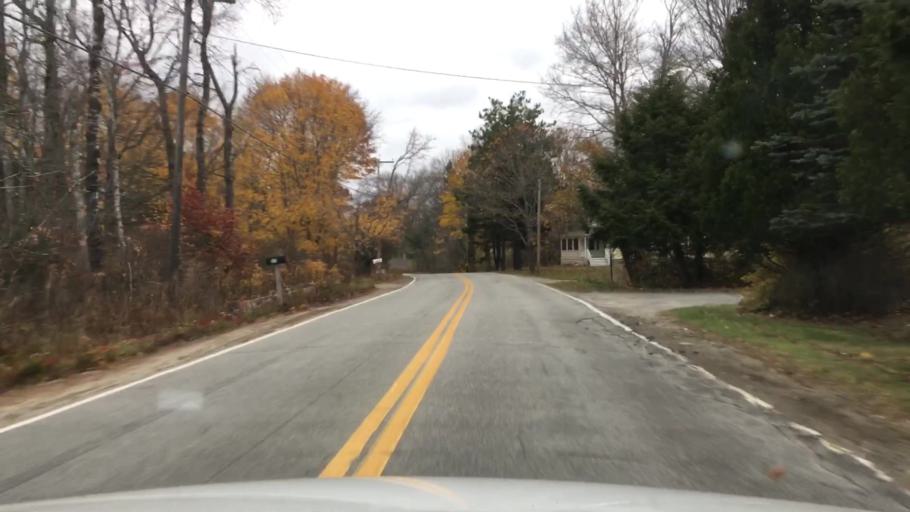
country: US
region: Maine
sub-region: Hancock County
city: Sedgwick
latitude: 44.2698
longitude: -68.5661
